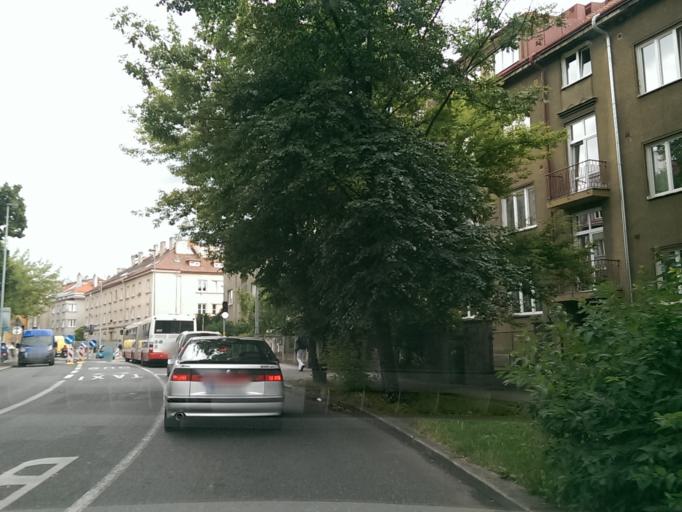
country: CZ
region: Praha
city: Branik
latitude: 50.0372
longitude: 14.4108
